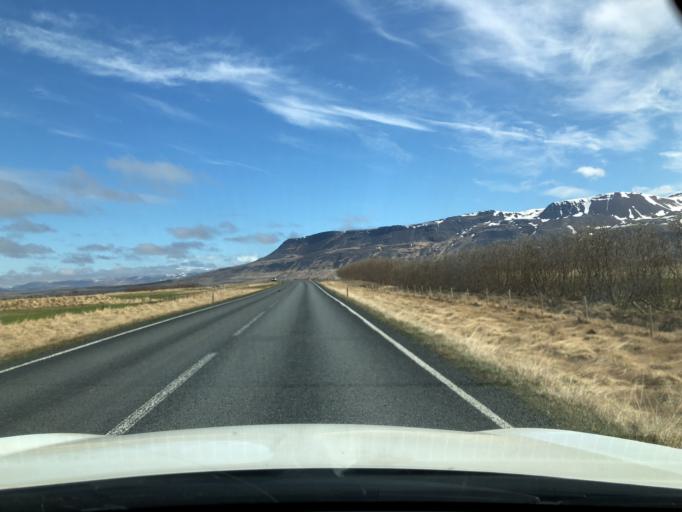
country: IS
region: Northwest
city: Saudarkrokur
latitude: 65.4931
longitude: -20.4137
